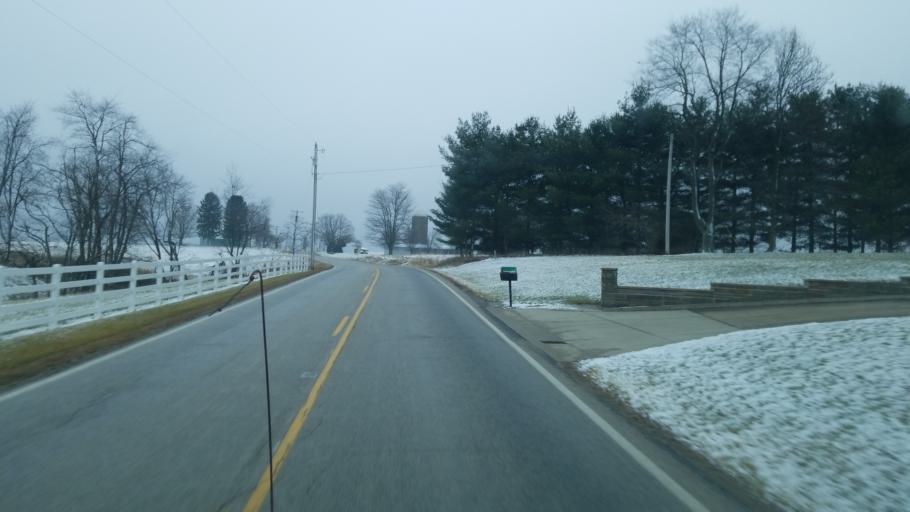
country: US
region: Ohio
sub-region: Ashland County
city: Loudonville
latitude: 40.7341
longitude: -82.1796
